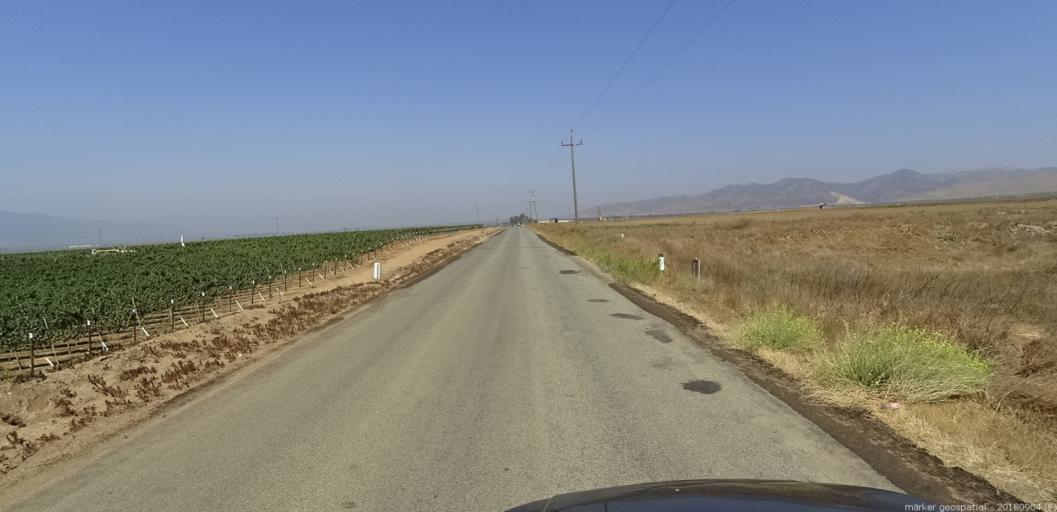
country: US
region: California
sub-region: Monterey County
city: Gonzales
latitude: 36.5295
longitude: -121.4200
